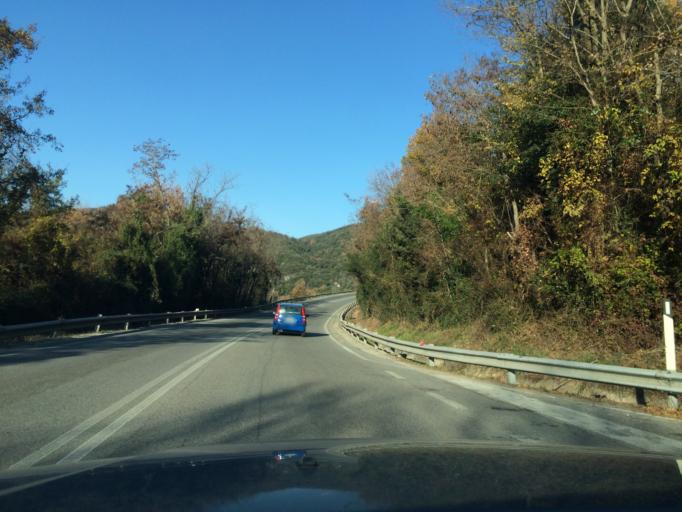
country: IT
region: Umbria
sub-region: Provincia di Terni
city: Fornole
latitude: 42.5344
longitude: 12.4754
